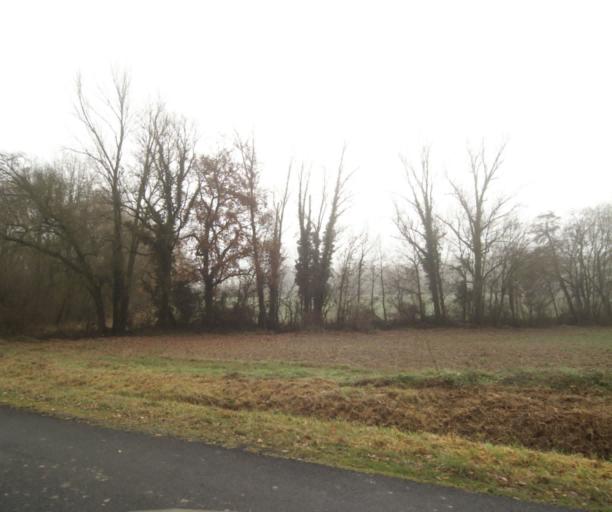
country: FR
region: Midi-Pyrenees
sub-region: Departement de la Haute-Garonne
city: Villaudric
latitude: 43.8212
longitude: 1.4564
